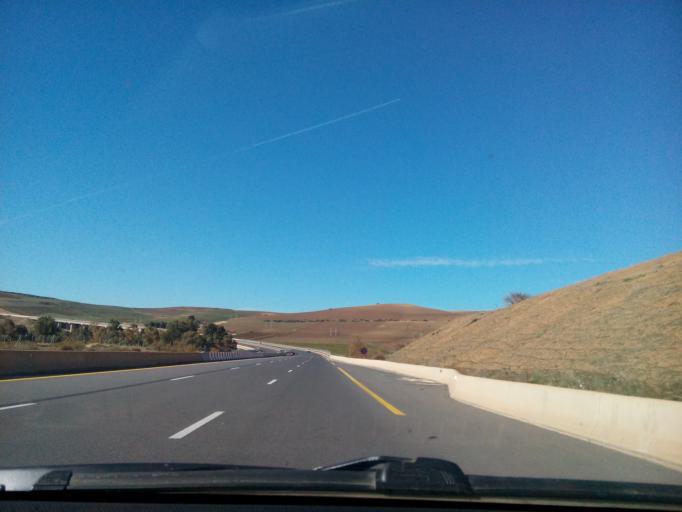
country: DZ
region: Tlemcen
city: Sidi Abdelli
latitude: 35.0396
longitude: -1.0607
